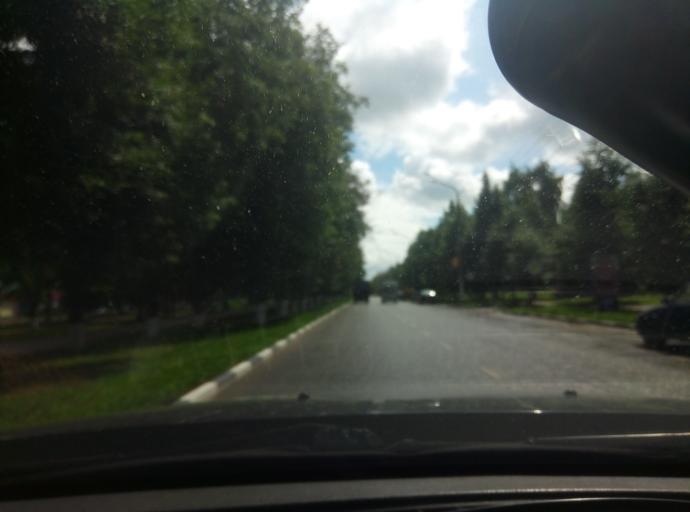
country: RU
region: Tula
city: Novomoskovsk
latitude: 54.0134
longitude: 38.2961
